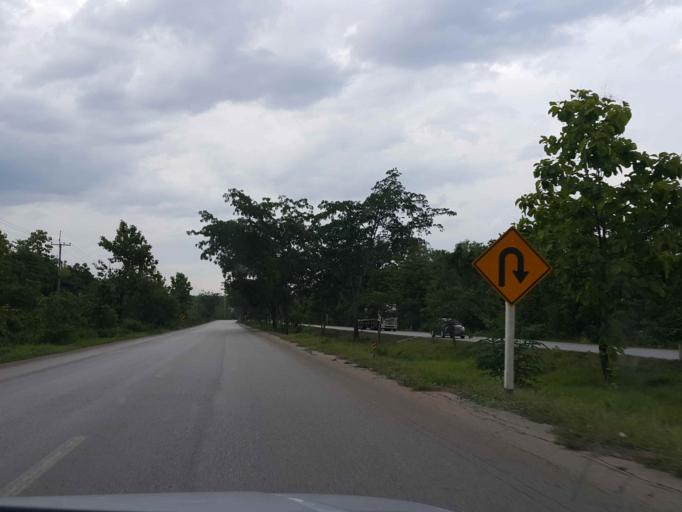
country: TH
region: Lampang
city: Soem Ngam
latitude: 18.0062
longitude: 99.3558
